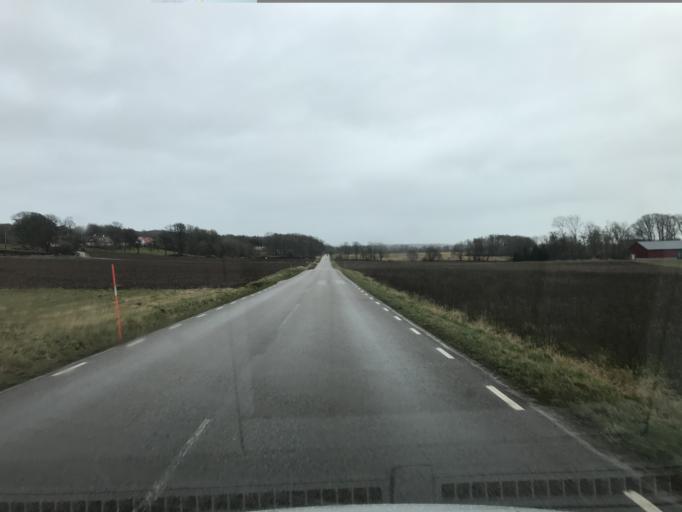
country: SE
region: Skane
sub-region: Bastads Kommun
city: Forslov
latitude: 56.3428
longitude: 12.8698
